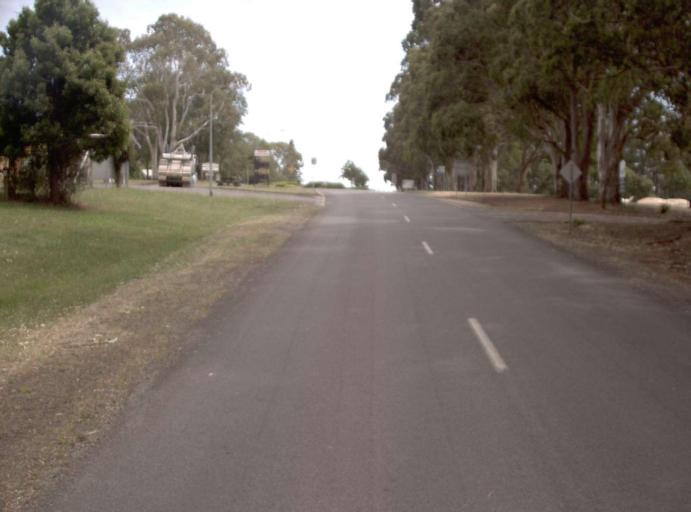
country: AU
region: Victoria
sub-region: Latrobe
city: Moe
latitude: -37.9573
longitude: 146.3991
